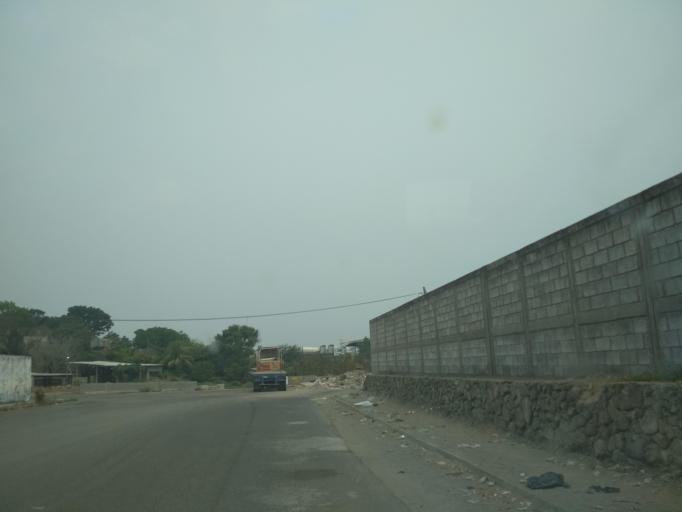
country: MX
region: Veracruz
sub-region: Veracruz
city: Rio Medio [Granja]
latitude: 19.2112
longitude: -96.2061
